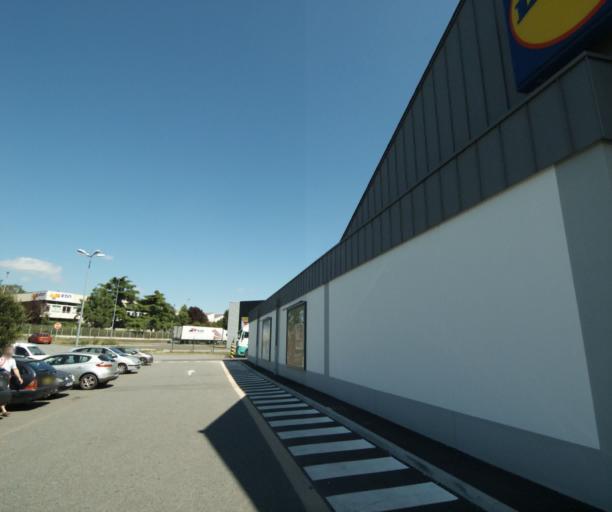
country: FR
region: Pays de la Loire
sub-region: Departement de la Mayenne
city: Laval
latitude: 48.0717
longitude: -0.7448
